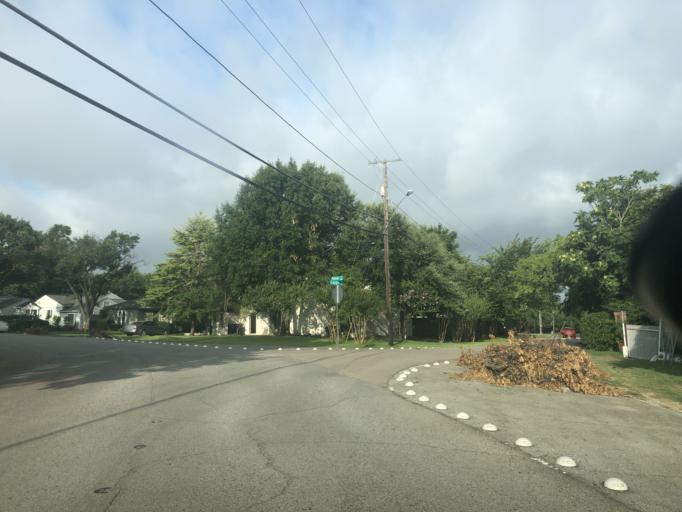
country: US
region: Texas
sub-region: Dallas County
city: University Park
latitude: 32.8562
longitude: -96.8398
